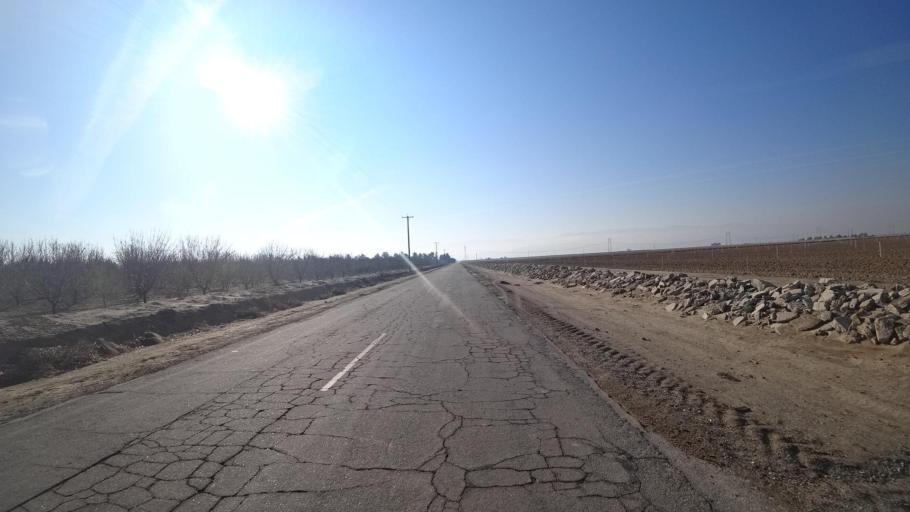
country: US
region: California
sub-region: Kern County
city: Weedpatch
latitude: 35.1348
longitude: -118.9677
